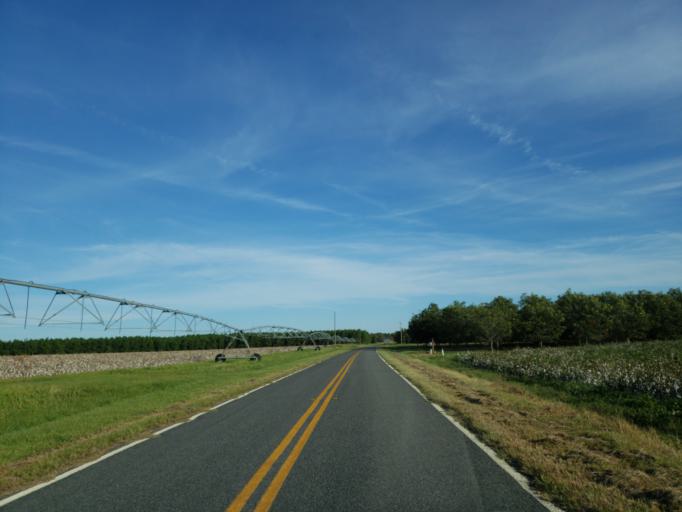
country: US
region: Georgia
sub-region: Dooly County
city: Vienna
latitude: 32.0646
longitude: -83.7732
